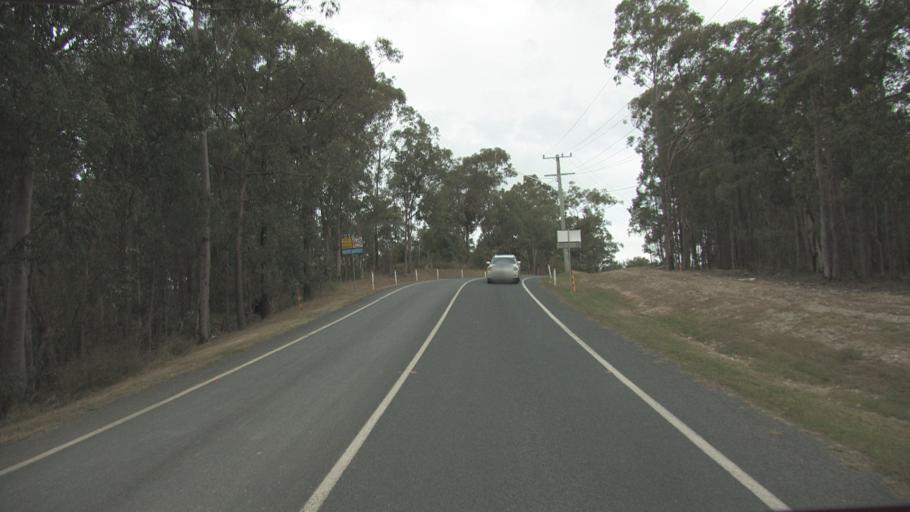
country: AU
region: Queensland
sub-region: Logan
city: Waterford West
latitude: -27.7212
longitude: 153.1596
